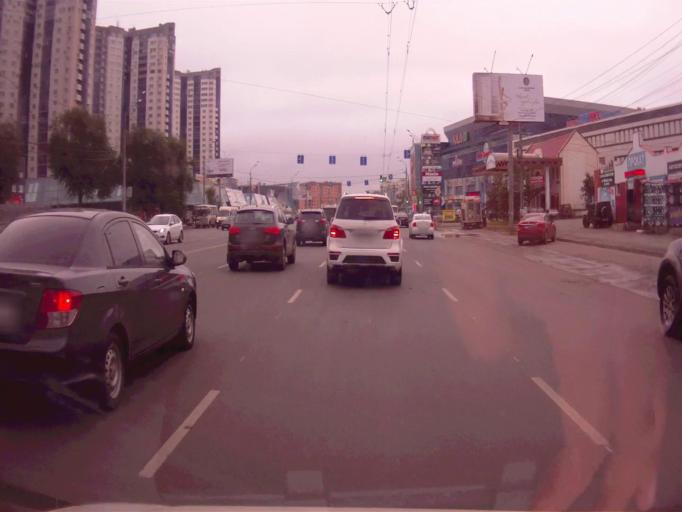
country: RU
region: Chelyabinsk
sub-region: Gorod Chelyabinsk
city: Chelyabinsk
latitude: 55.1691
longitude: 61.3760
